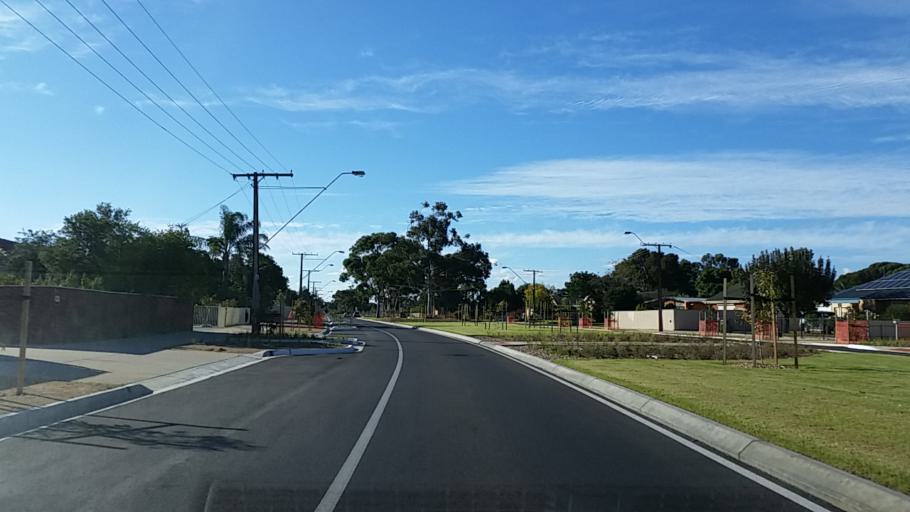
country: AU
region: South Australia
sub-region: Playford
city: Smithfield
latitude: -34.6895
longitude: 138.6695
